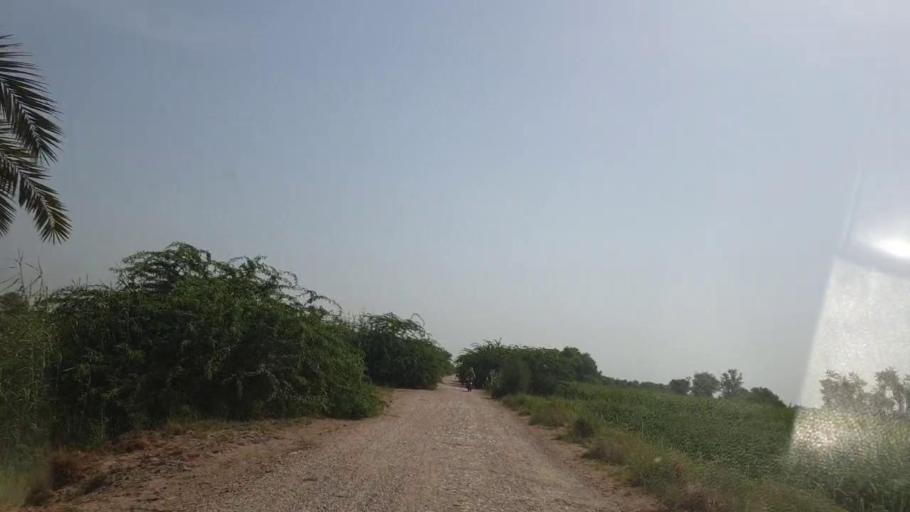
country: PK
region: Sindh
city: Gambat
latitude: 27.3717
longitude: 68.5687
